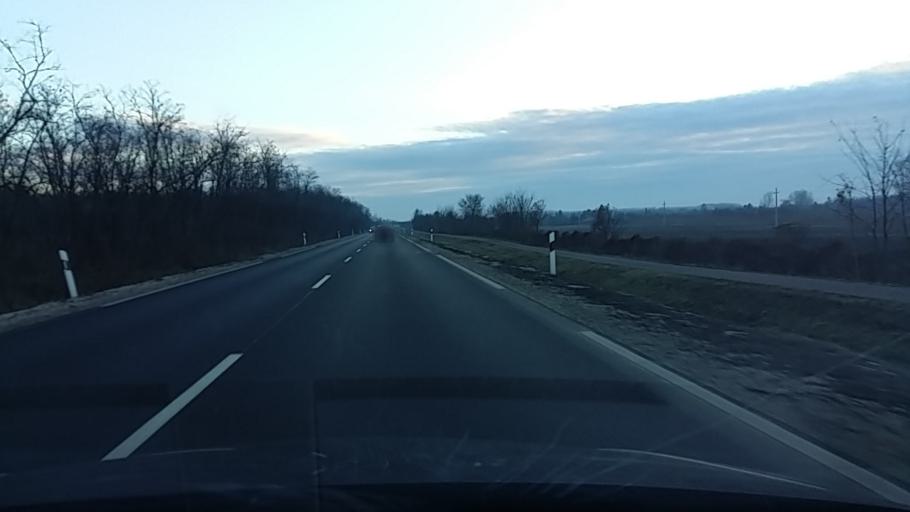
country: HU
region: Hajdu-Bihar
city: Hajduhadhaz
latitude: 47.6296
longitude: 21.6596
